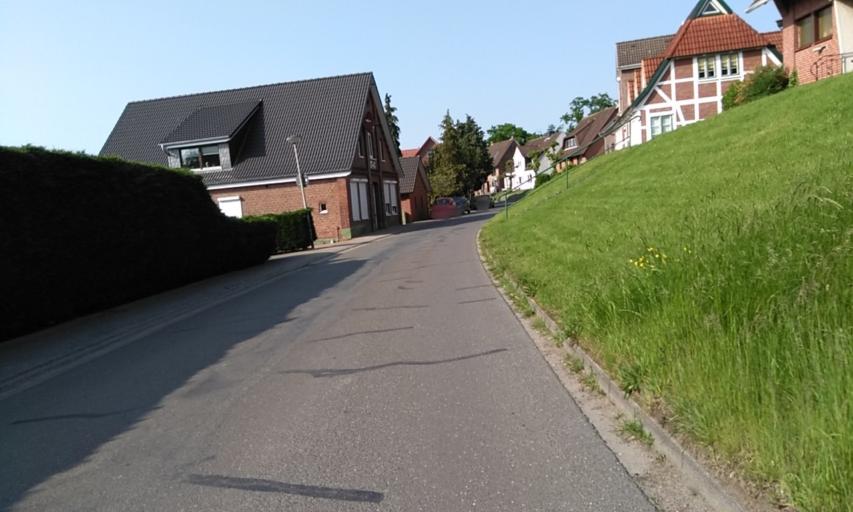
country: DE
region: Lower Saxony
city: Jork
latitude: 53.5082
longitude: 9.7300
